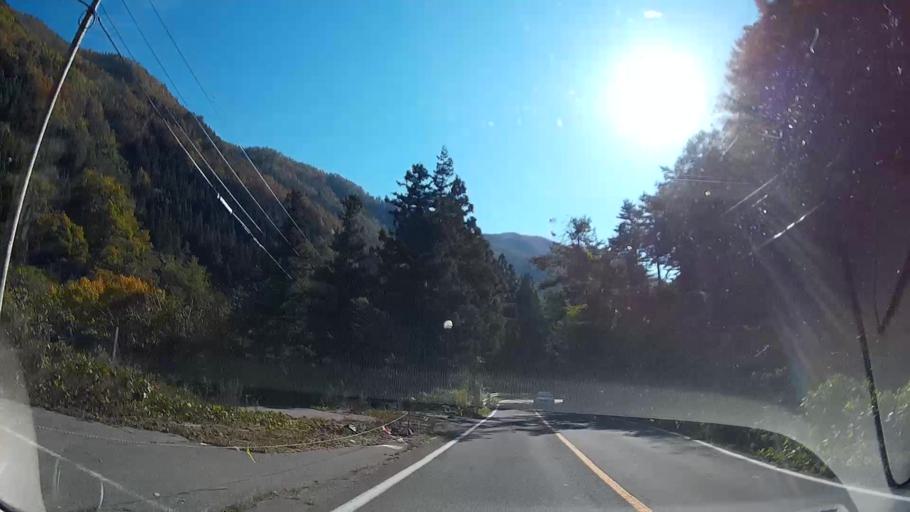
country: JP
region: Nagano
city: Toyoshina
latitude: 36.1755
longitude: 137.7808
